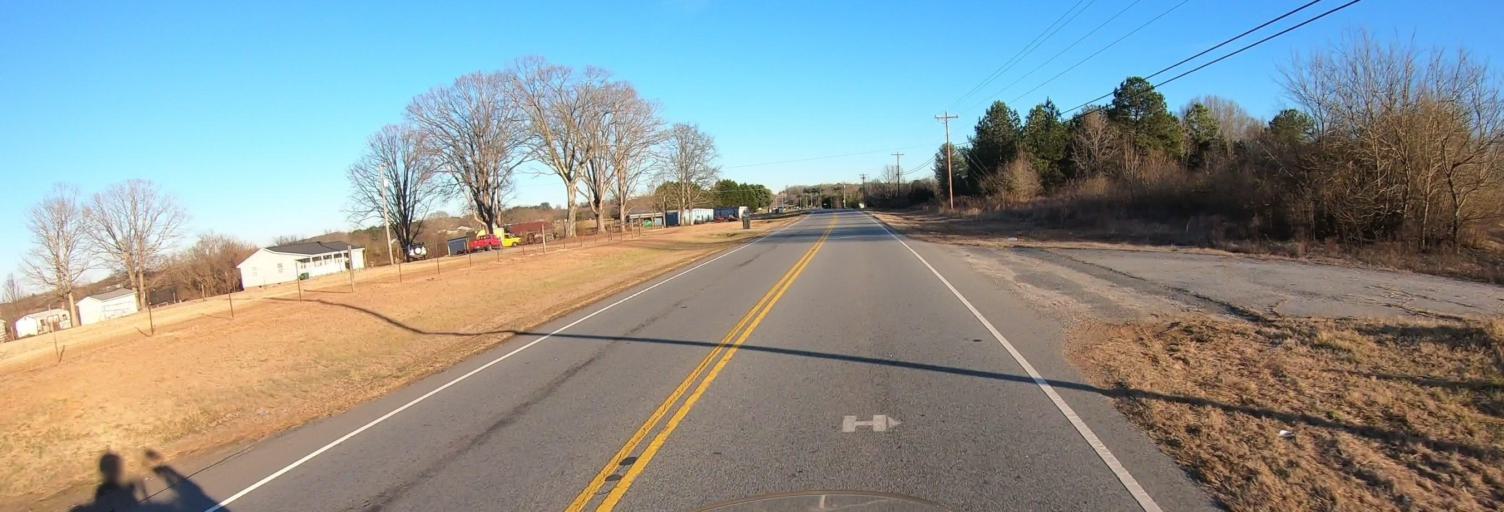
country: US
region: South Carolina
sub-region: Spartanburg County
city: Mayo
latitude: 35.1306
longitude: -81.7956
